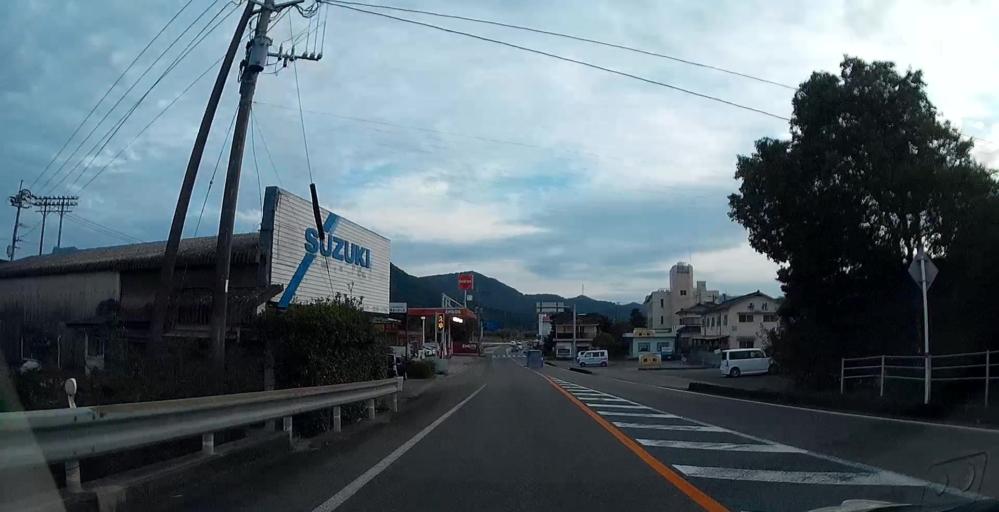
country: JP
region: Kumamoto
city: Yatsushiro
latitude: 32.5156
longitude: 130.4290
